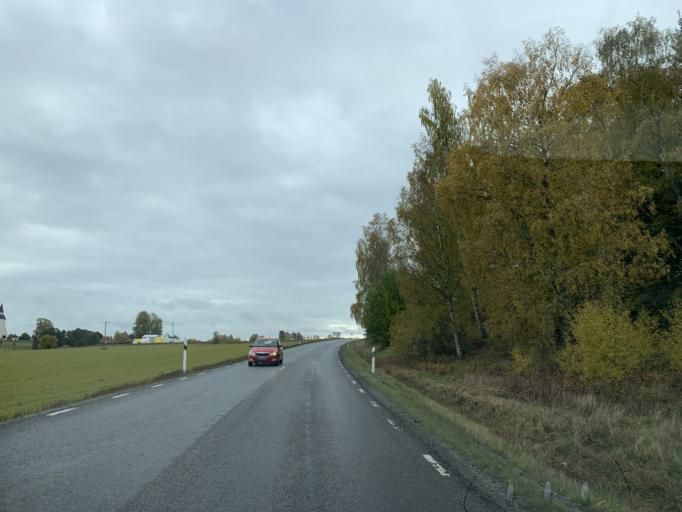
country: SE
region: Stockholm
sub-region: Nynashamns Kommun
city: Osmo
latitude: 59.0134
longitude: 17.8057
